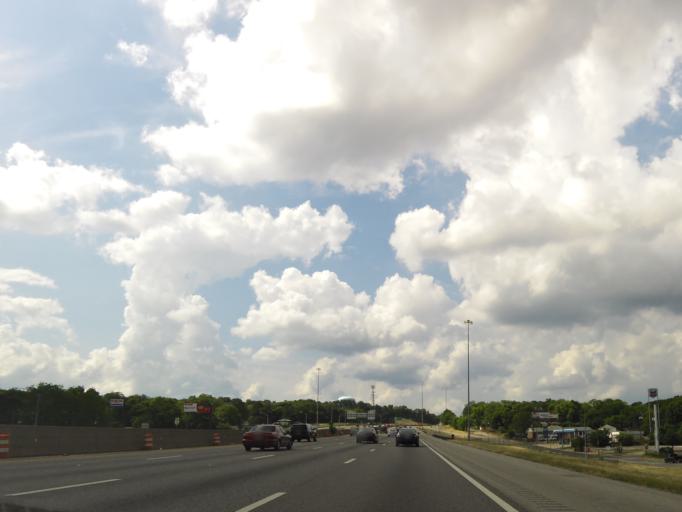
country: US
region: Alabama
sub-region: Jefferson County
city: Birmingham
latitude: 33.5492
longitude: -86.8290
